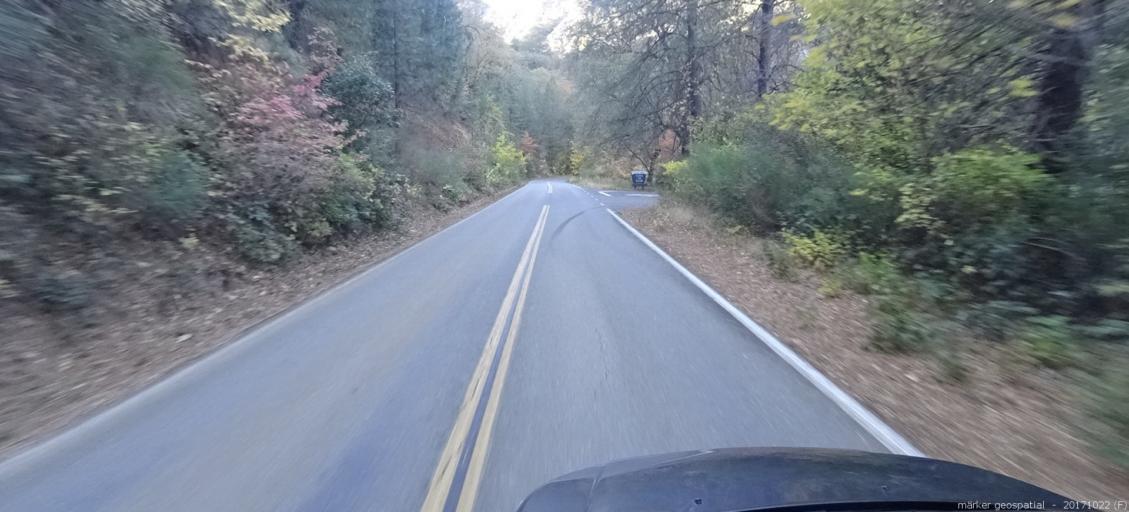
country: US
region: California
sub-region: Shasta County
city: Shasta Lake
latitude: 40.9154
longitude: -122.2446
